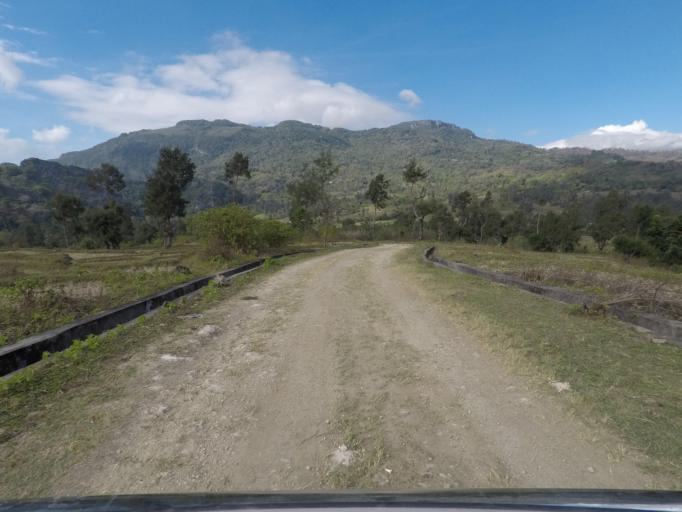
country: TL
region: Baucau
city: Venilale
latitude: -8.6548
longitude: 126.3947
